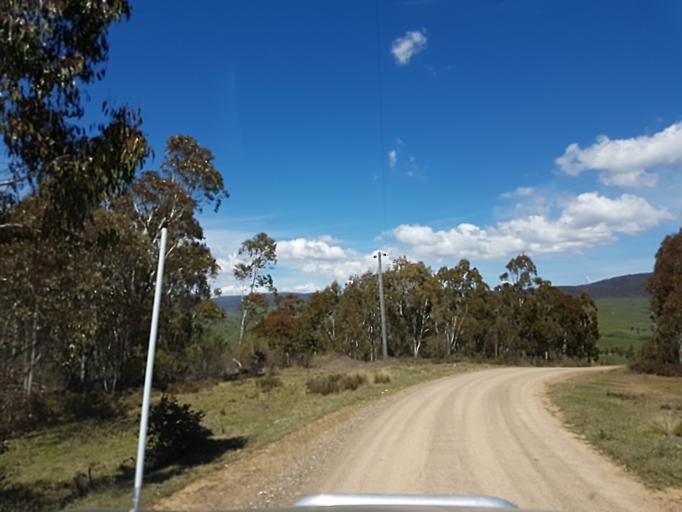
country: AU
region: Victoria
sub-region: Alpine
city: Mount Beauty
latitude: -37.0856
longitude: 147.4071
